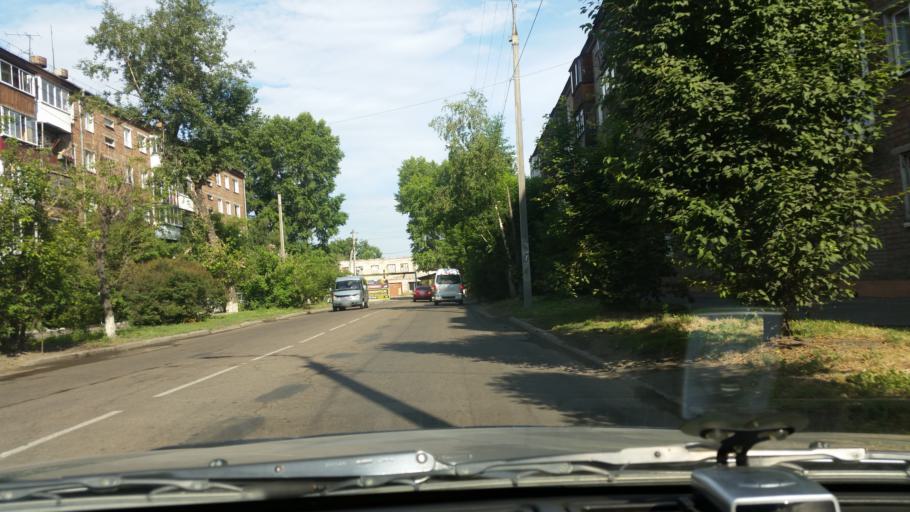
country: RU
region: Irkutsk
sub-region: Irkutskiy Rayon
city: Irkutsk
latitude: 52.2863
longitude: 104.3096
